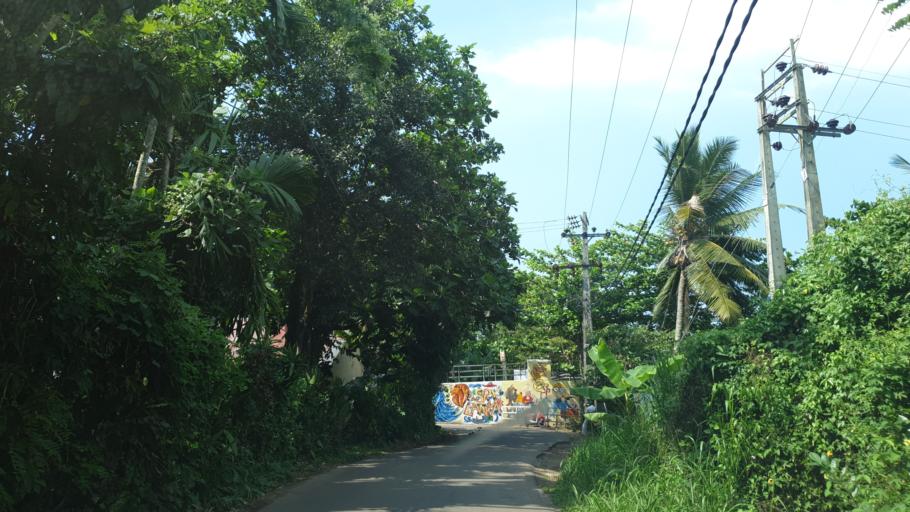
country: LK
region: Western
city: Panadura
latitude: 6.7422
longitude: 79.9466
